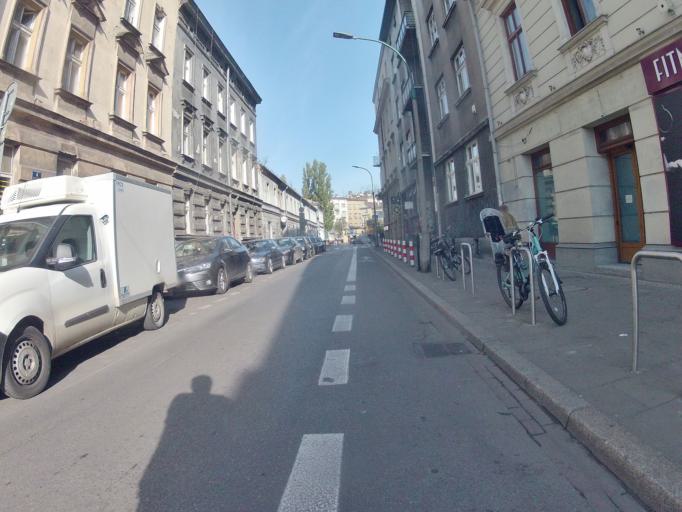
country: PL
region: Lesser Poland Voivodeship
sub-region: Krakow
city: Krakow
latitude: 50.0639
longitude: 19.9278
